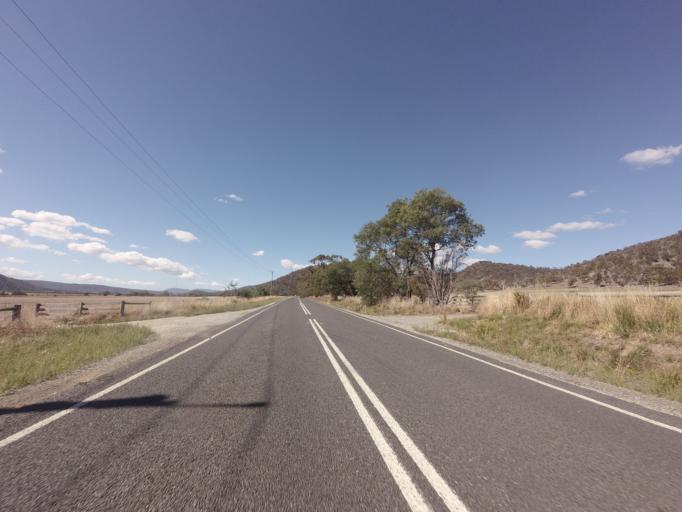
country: AU
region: Tasmania
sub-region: Break O'Day
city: St Helens
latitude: -41.6926
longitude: 147.8697
